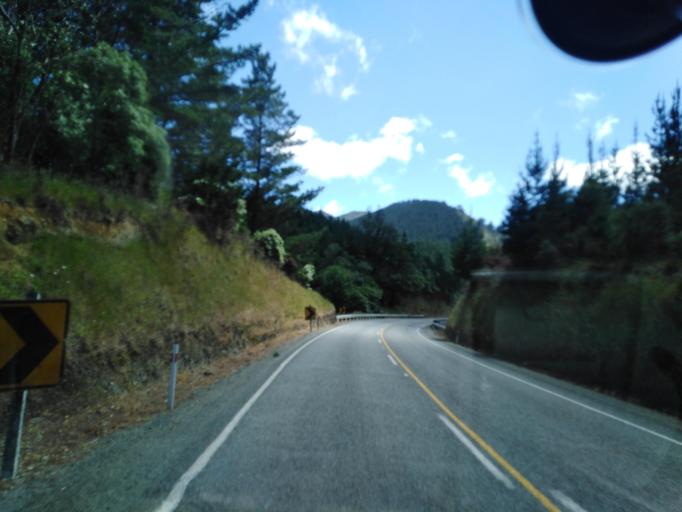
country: NZ
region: Nelson
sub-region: Nelson City
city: Nelson
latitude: -41.1771
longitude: 173.5609
